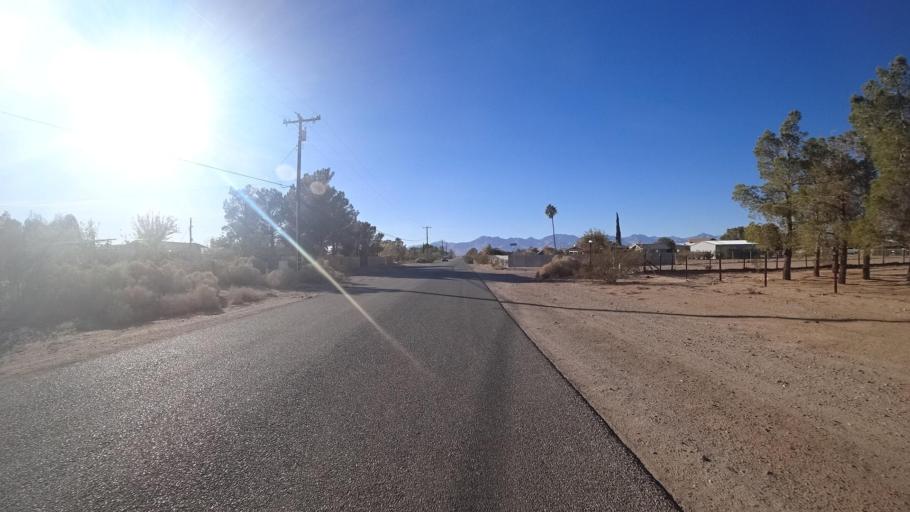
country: US
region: California
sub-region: Kern County
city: Ridgecrest
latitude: 35.6443
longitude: -117.7020
